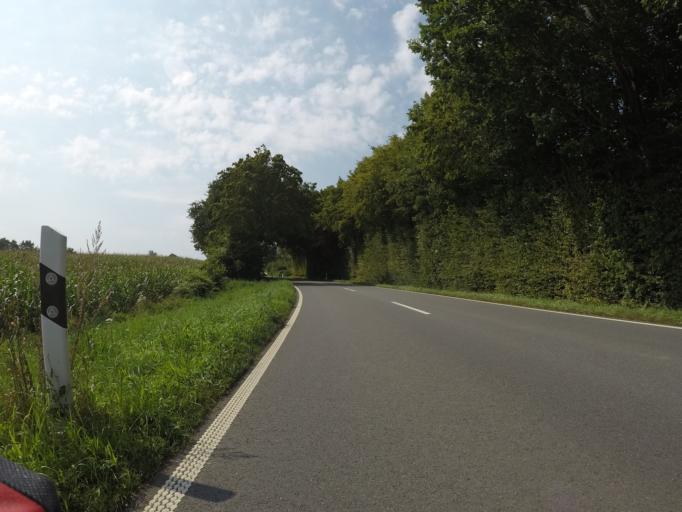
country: DE
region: Schleswig-Holstein
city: Huttblek
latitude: 53.8410
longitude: 10.0512
